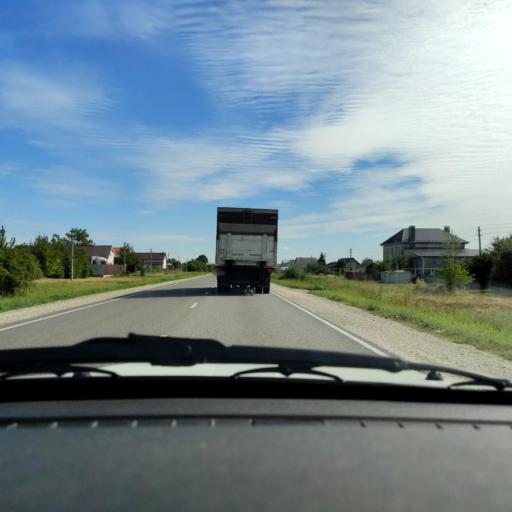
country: RU
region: Voronezj
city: Orlovo
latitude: 51.7408
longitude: 39.5733
